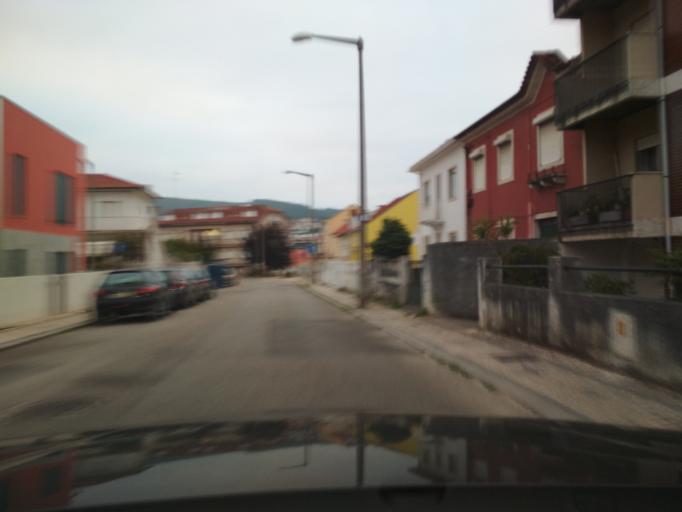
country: PT
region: Coimbra
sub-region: Coimbra
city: Coimbra
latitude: 40.1979
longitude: -8.4049
